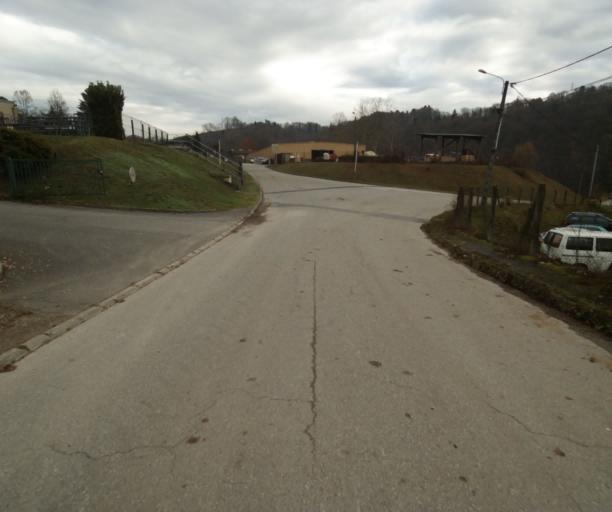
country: FR
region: Limousin
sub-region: Departement de la Correze
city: Tulle
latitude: 45.2424
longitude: 1.7373
